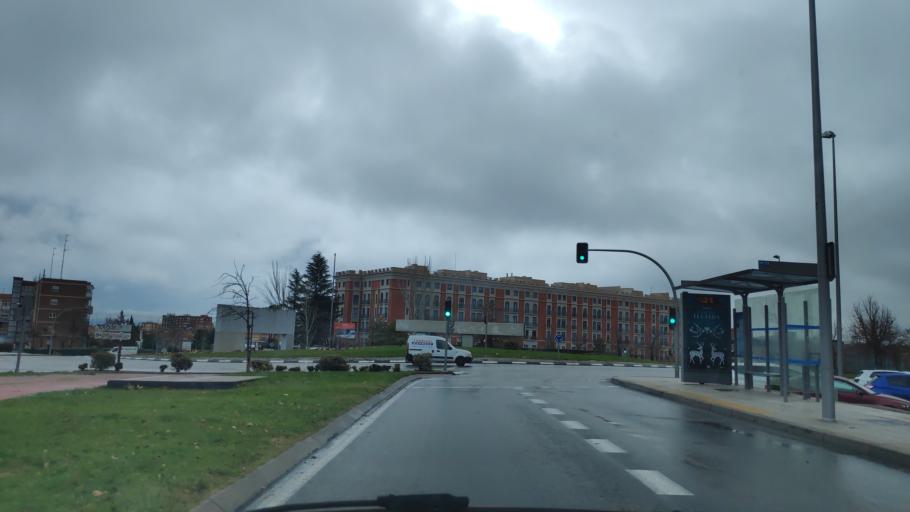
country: ES
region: Madrid
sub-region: Provincia de Madrid
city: Pinar de Chamartin
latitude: 40.4711
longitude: -3.6590
